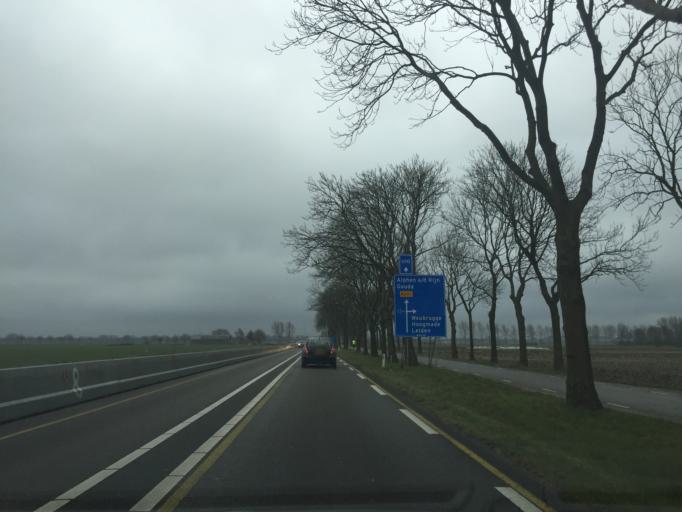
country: NL
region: South Holland
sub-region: Gemeente Alphen aan den Rijn
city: Alphen aan den Rijn
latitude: 52.1734
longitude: 4.6694
